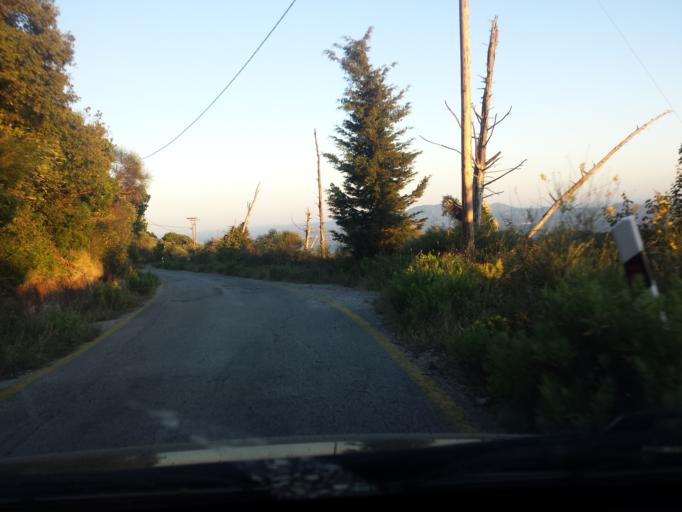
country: GR
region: Ionian Islands
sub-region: Nomos Kerkyras
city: Acharavi
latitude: 39.7259
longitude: 19.8350
